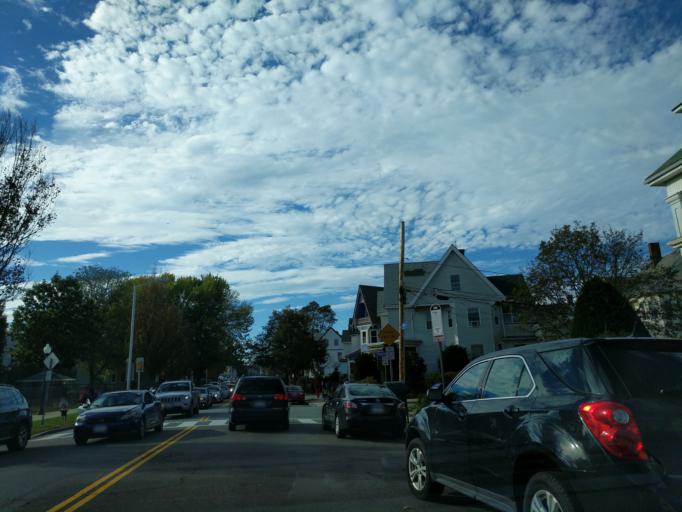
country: US
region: Massachusetts
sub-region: Middlesex County
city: Malden
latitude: 42.4225
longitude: -71.0606
